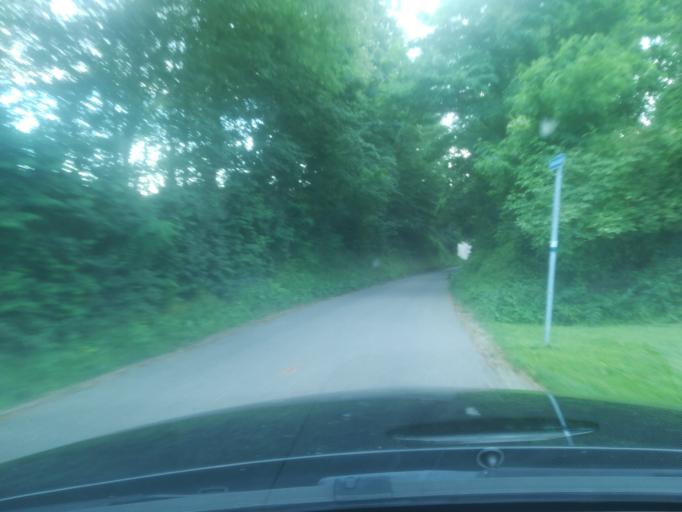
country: AT
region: Upper Austria
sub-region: Politischer Bezirk Urfahr-Umgebung
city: Ottensheim
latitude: 48.3220
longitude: 14.1820
